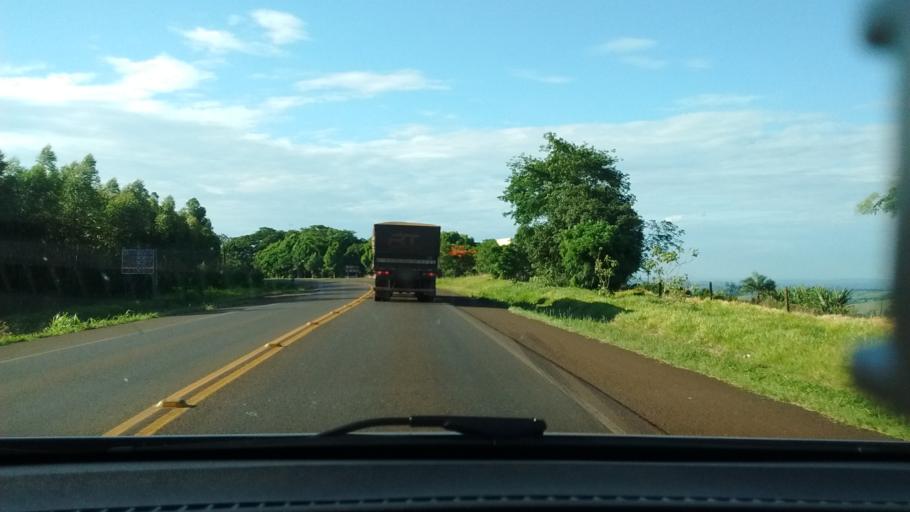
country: BR
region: Parana
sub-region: Cascavel
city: Cascavel
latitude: -25.2482
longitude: -53.5790
